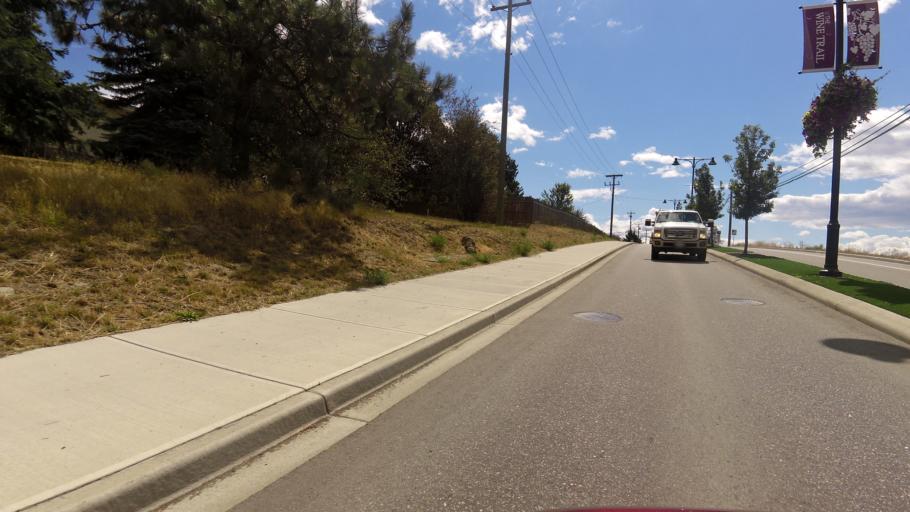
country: CA
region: British Columbia
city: West Kelowna
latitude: 49.8656
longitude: -119.5550
